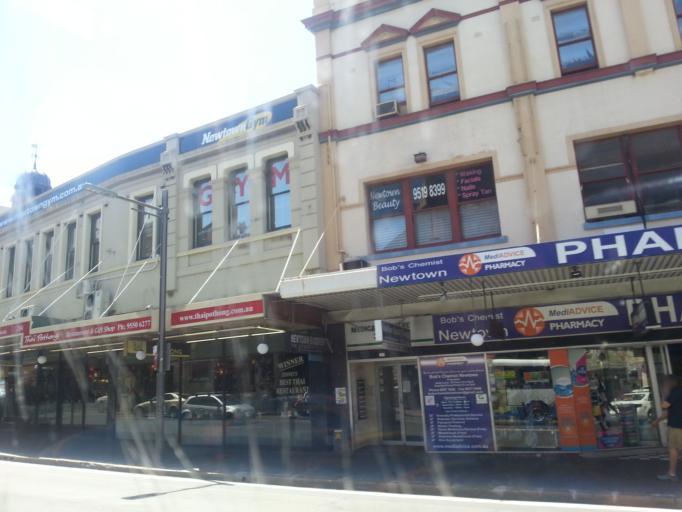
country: AU
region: New South Wales
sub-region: Marrickville
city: Newtown
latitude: -33.8968
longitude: 151.1794
